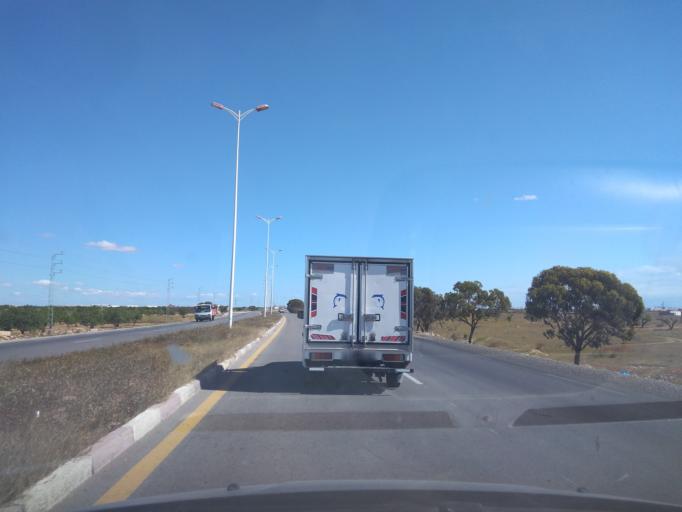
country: TN
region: Safaqis
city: Sfax
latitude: 34.8342
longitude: 10.7308
